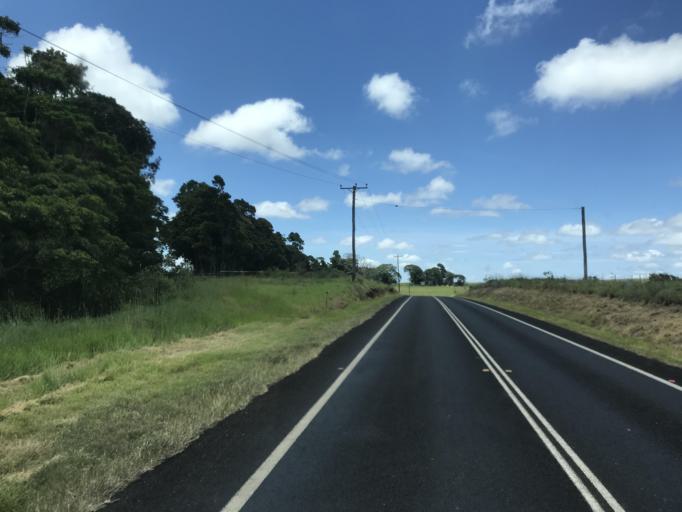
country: AU
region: Queensland
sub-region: Tablelands
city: Ravenshoe
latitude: -17.4944
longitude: 145.4757
